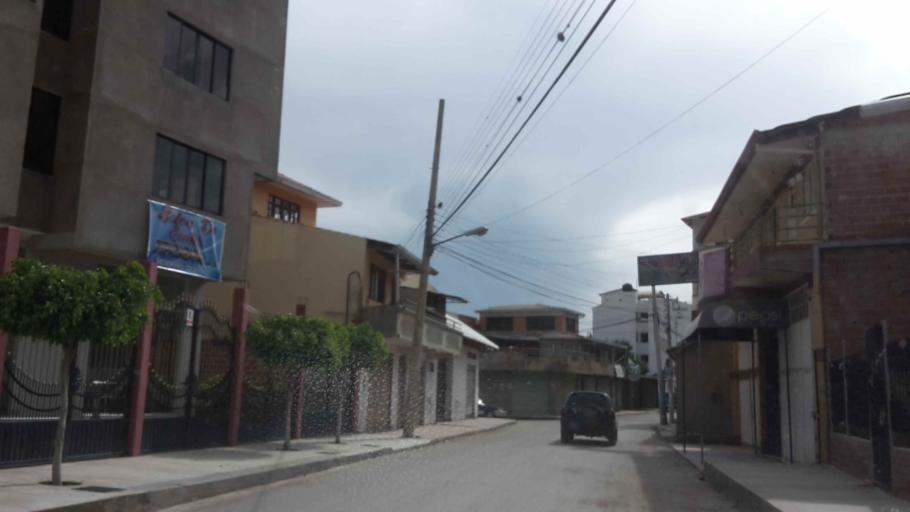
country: BO
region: Cochabamba
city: Cochabamba
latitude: -17.3377
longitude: -66.2634
